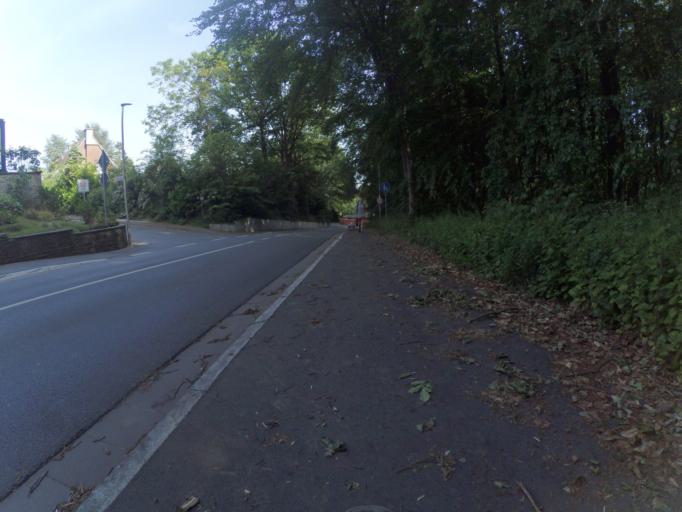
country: DE
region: North Rhine-Westphalia
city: Ibbenburen
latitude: 52.2798
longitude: 7.7499
